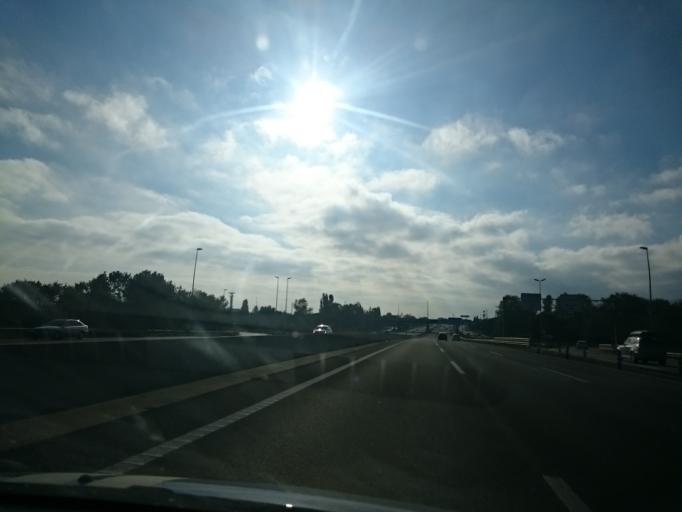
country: ES
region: Catalonia
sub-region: Provincia de Barcelona
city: Gava
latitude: 41.2939
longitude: 2.0119
